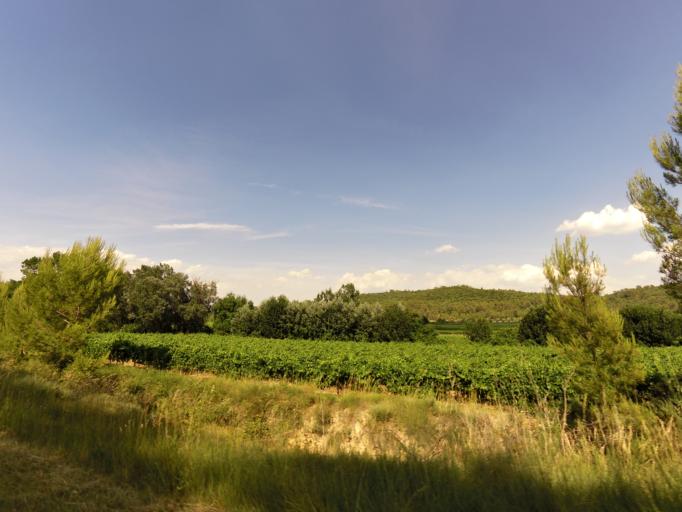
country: FR
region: Languedoc-Roussillon
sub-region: Departement du Gard
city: Quissac
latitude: 43.8591
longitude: 4.0171
